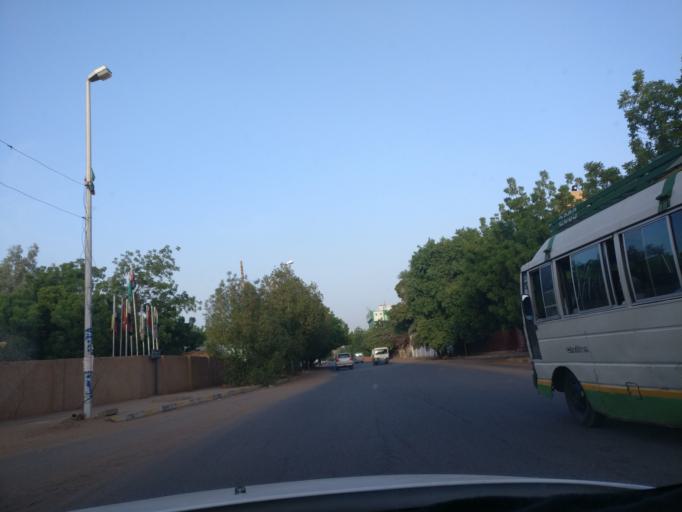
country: SD
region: Khartoum
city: Omdurman
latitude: 15.6035
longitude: 32.5072
